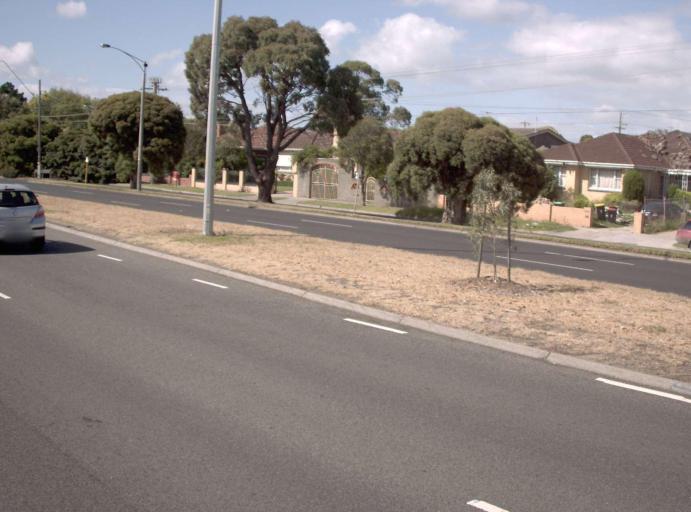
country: AU
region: Victoria
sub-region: Bayside
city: Highett
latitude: -37.9440
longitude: 145.0426
